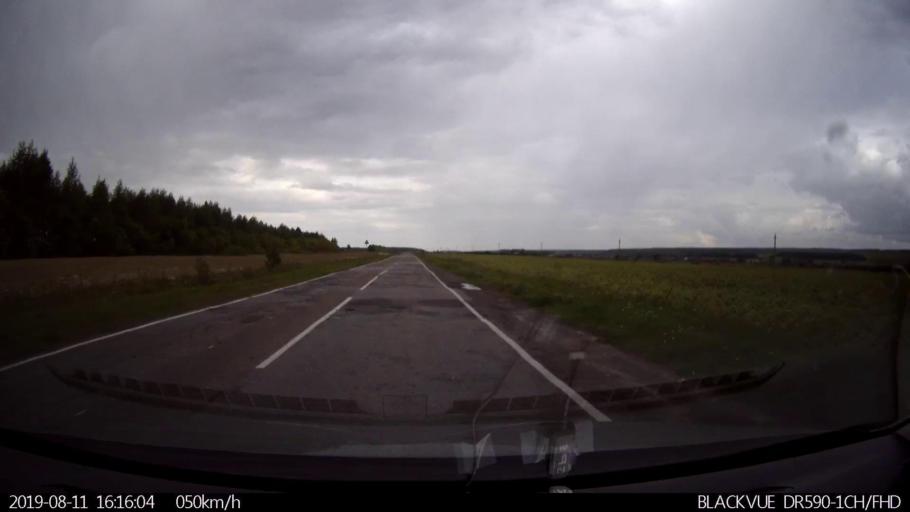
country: RU
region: Ulyanovsk
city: Mayna
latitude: 54.0383
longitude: 47.6230
